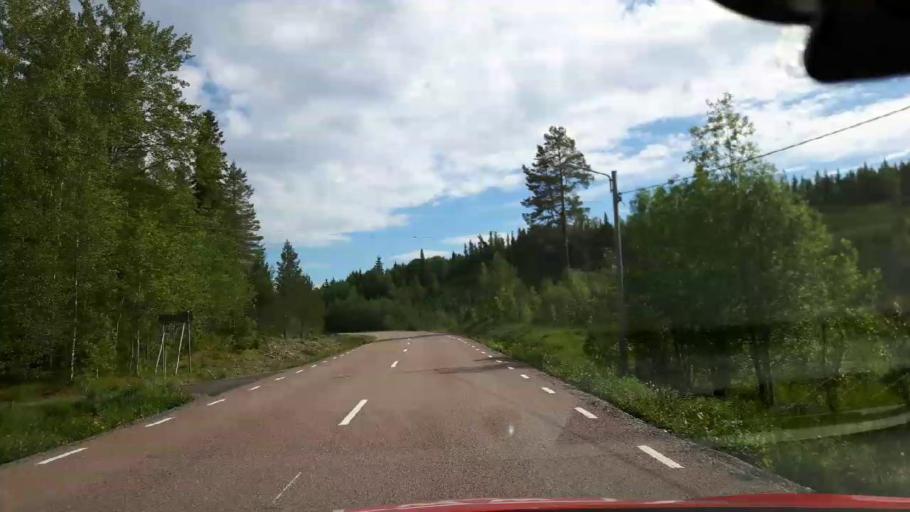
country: SE
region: Jaemtland
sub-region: Krokoms Kommun
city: Valla
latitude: 63.9288
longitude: 14.2110
